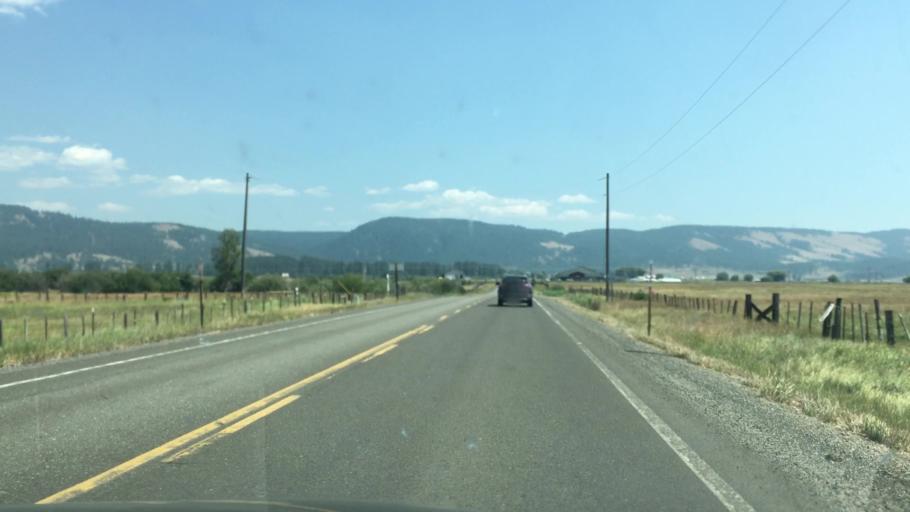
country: US
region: Idaho
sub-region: Valley County
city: McCall
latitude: 44.9703
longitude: -116.2775
